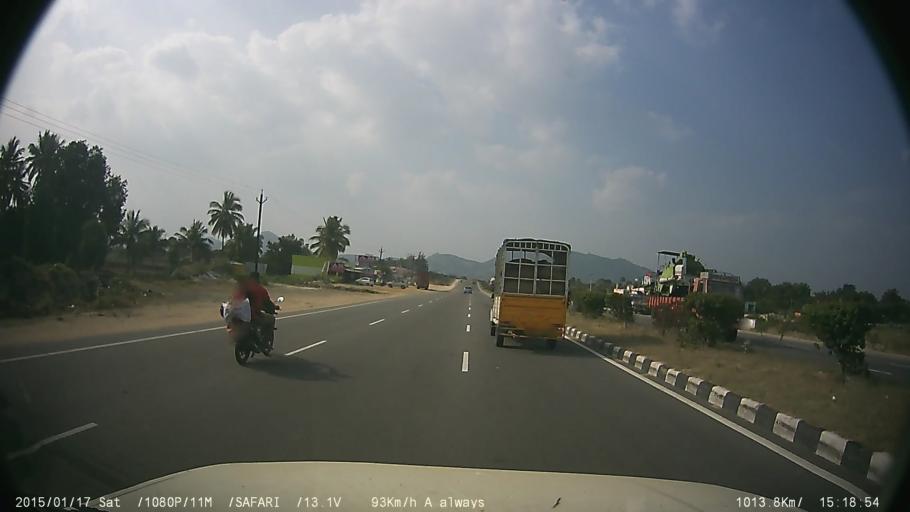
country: IN
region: Tamil Nadu
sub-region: Krishnagiri
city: Krishnagiri
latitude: 12.5900
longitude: 78.1423
